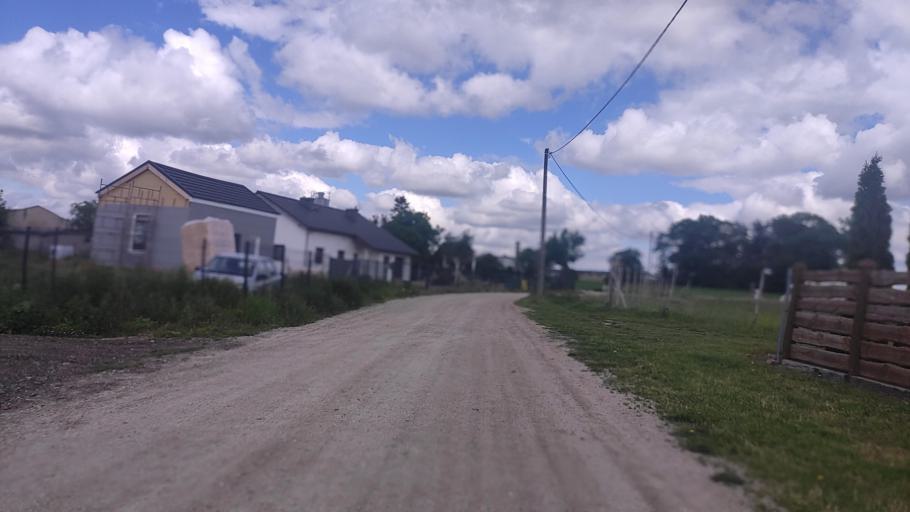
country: PL
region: Greater Poland Voivodeship
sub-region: Powiat poznanski
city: Kostrzyn
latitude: 52.4136
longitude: 17.1737
